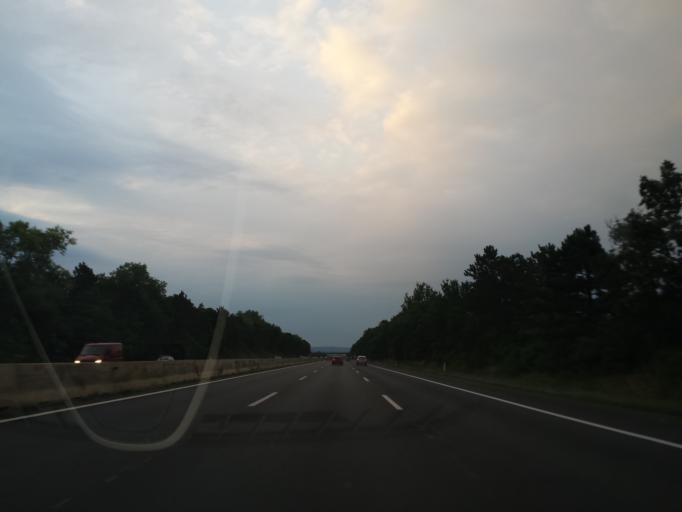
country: AT
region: Lower Austria
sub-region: Politischer Bezirk Baden
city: Leobersdorf
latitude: 47.9020
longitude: 16.2076
